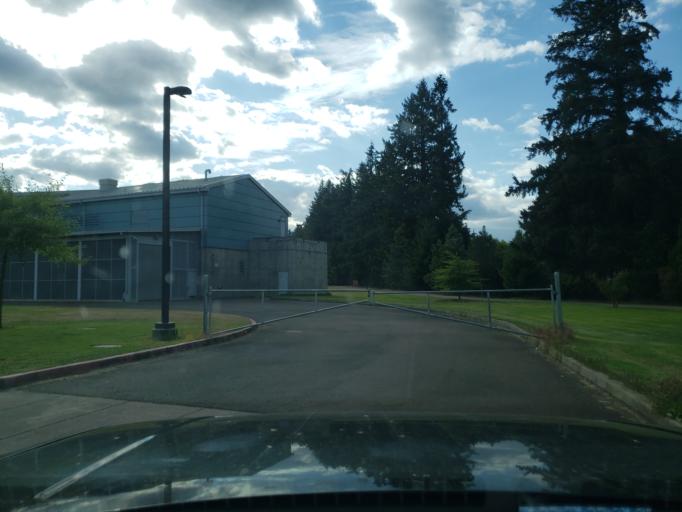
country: US
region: Oregon
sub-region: Marion County
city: Keizer
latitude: 44.9709
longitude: -123.0308
